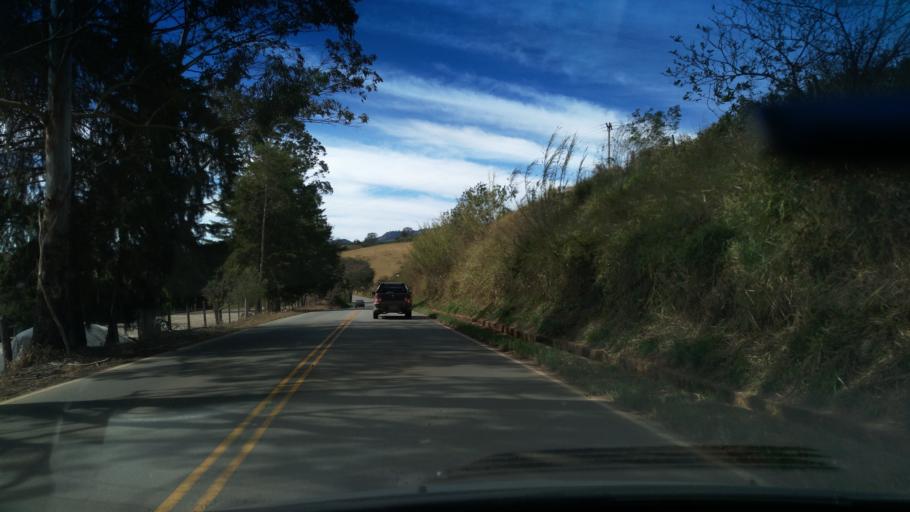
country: BR
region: Minas Gerais
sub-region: Andradas
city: Andradas
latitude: -22.0668
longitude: -46.4608
